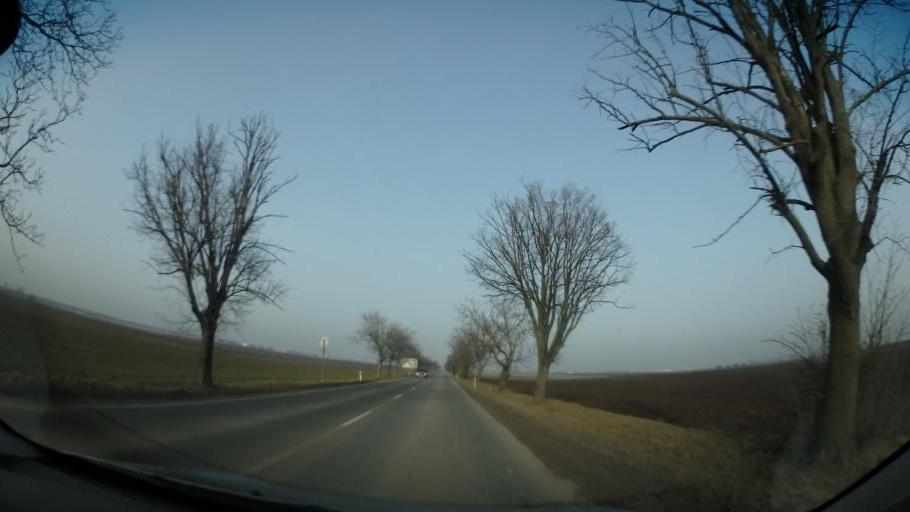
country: CZ
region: South Moravian
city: Rajhrad
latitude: 49.0696
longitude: 16.5746
